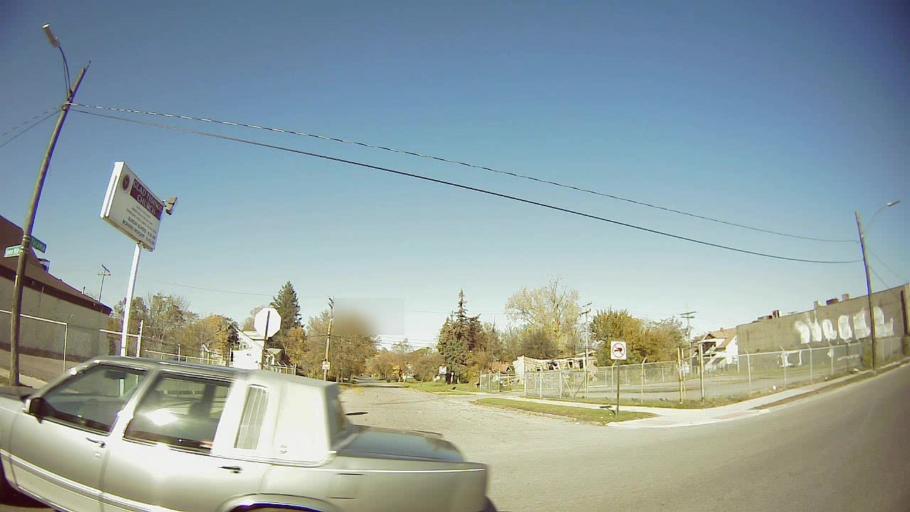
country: US
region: Michigan
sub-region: Wayne County
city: Highland Park
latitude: 42.4323
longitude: -83.0969
